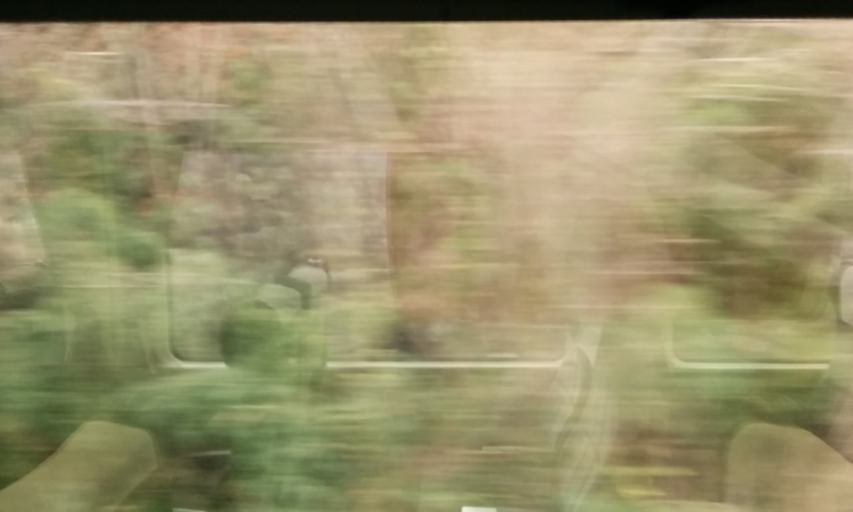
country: JP
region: Nagano
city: Nagano-shi
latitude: 36.5421
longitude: 138.1004
